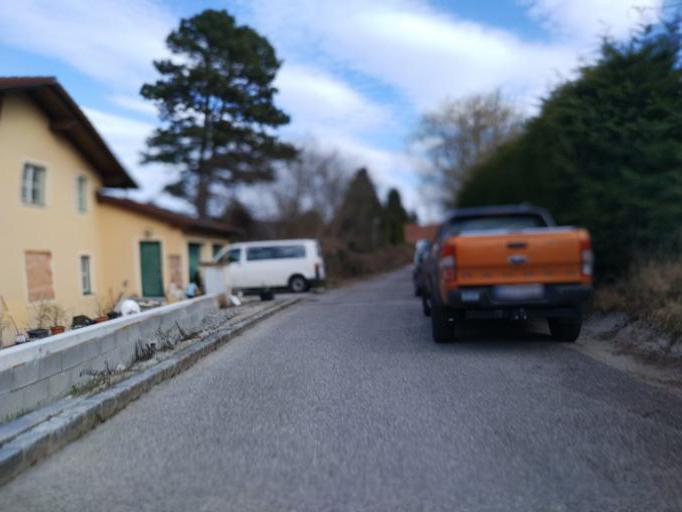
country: AT
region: Lower Austria
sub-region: Politischer Bezirk Wien-Umgebung
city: Gablitz
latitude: 48.2241
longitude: 16.1503
